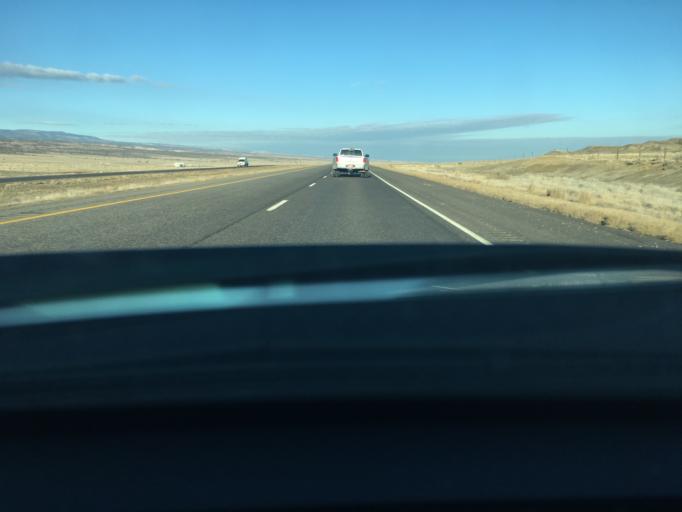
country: US
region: Colorado
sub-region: Mesa County
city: Palisade
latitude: 38.8731
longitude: -108.3403
